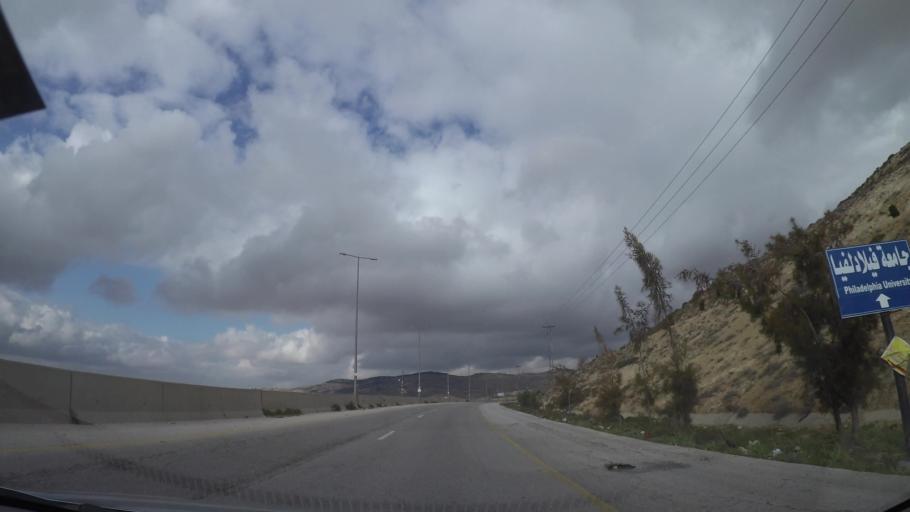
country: JO
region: Amman
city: Al Jubayhah
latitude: 32.0813
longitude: 35.8797
